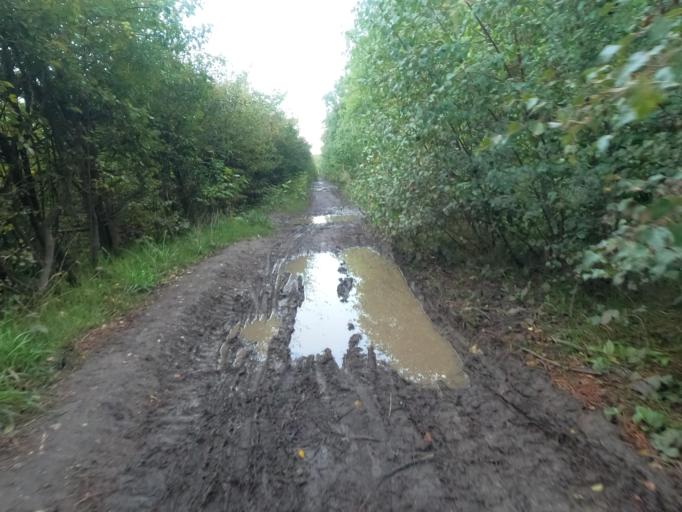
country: GB
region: England
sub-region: Northumberland
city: Seghill
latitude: 55.0714
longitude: -1.5479
